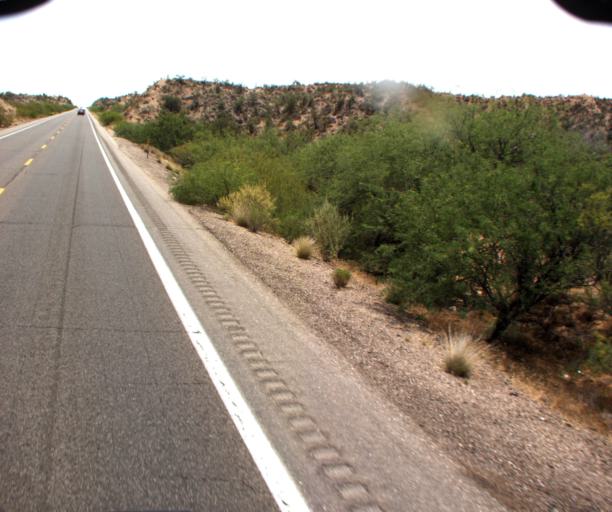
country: US
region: Arizona
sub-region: Gila County
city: San Carlos
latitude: 33.3423
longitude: -110.6062
